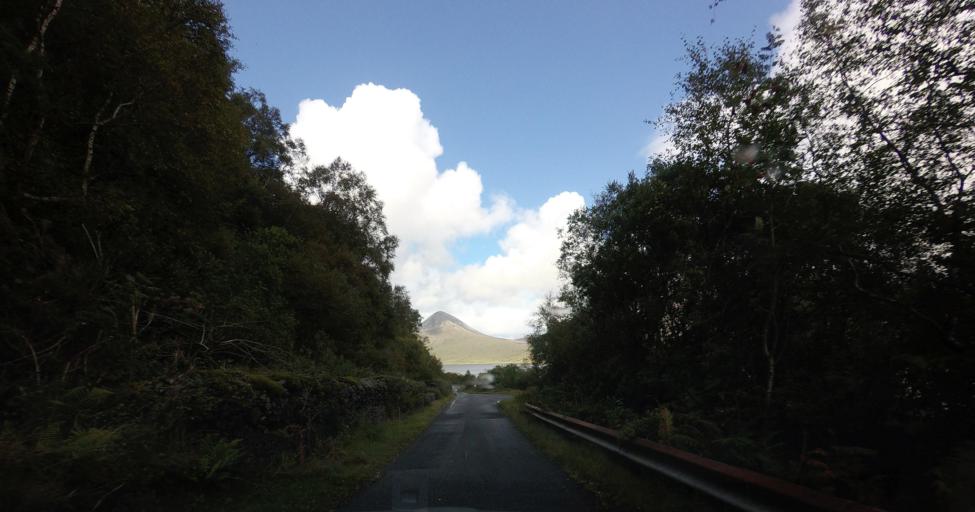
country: GB
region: Scotland
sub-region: Highland
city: Portree
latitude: 57.2016
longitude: -6.0270
